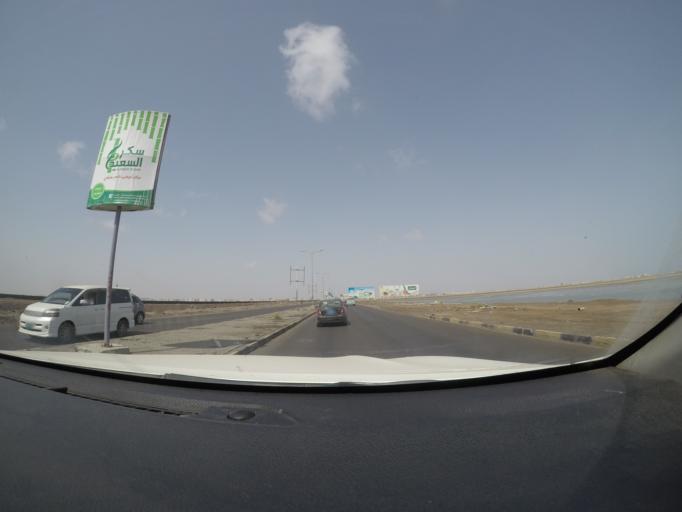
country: YE
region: Aden
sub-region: Khur Maksar
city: Khawr Maksar
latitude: 12.8306
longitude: 45.0304
